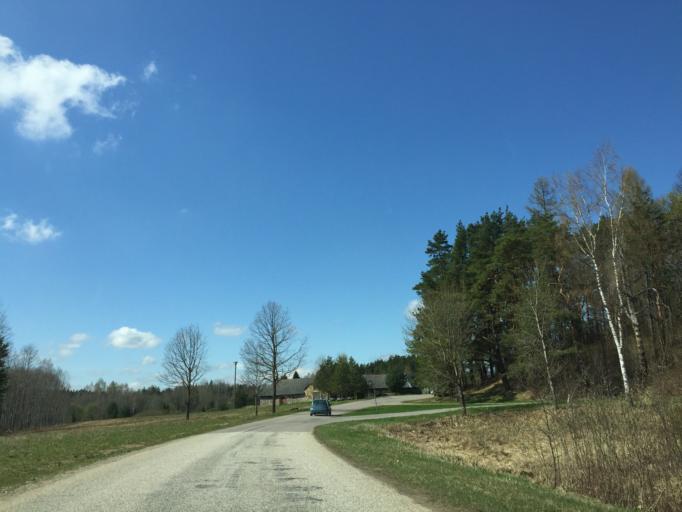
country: EE
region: Tartu
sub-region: Elva linn
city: Elva
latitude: 58.1529
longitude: 26.2274
